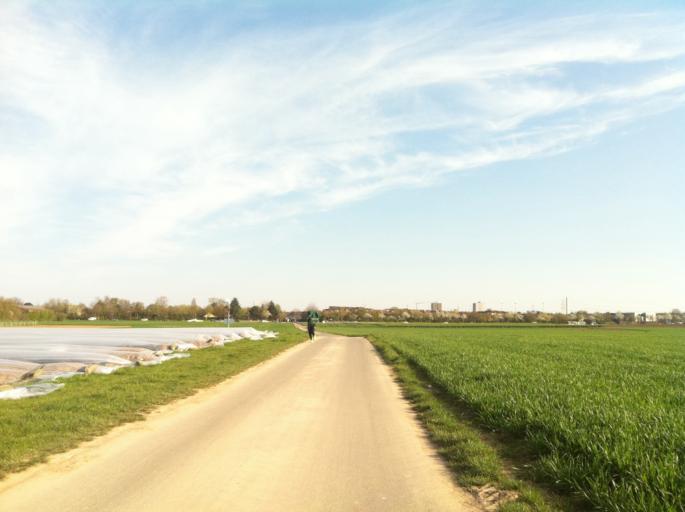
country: DE
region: Rheinland-Pfalz
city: Klein-Winternheim
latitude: 49.9764
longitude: 8.2287
